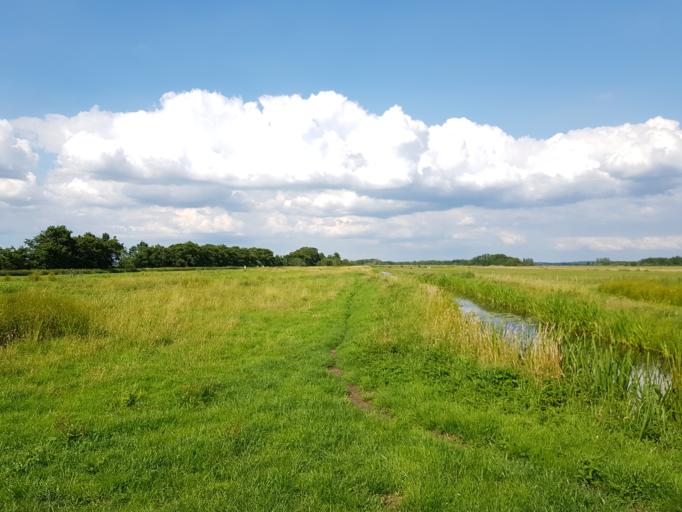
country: NL
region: North Holland
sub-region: Gemeente Wijdemeren
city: Oud-Loosdrecht
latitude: 52.1634
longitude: 5.1022
